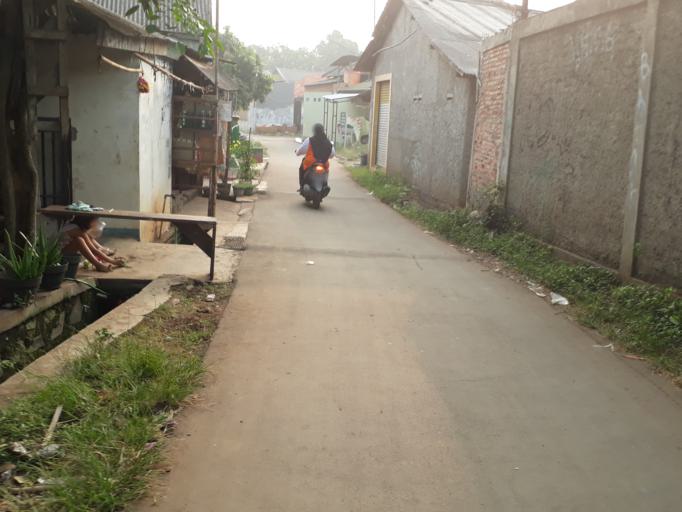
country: ID
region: West Java
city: Bekasi
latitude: -6.2478
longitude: 107.0680
